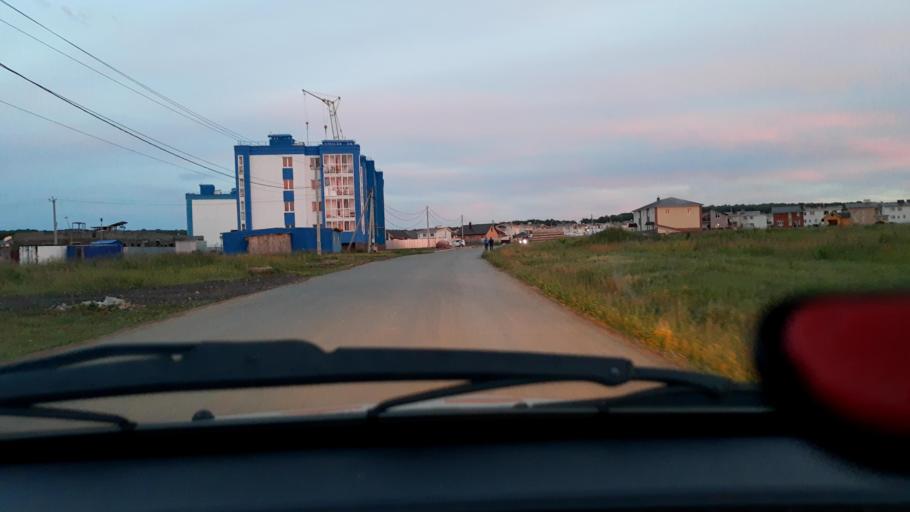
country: RU
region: Bashkortostan
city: Avdon
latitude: 54.4843
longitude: 55.8806
